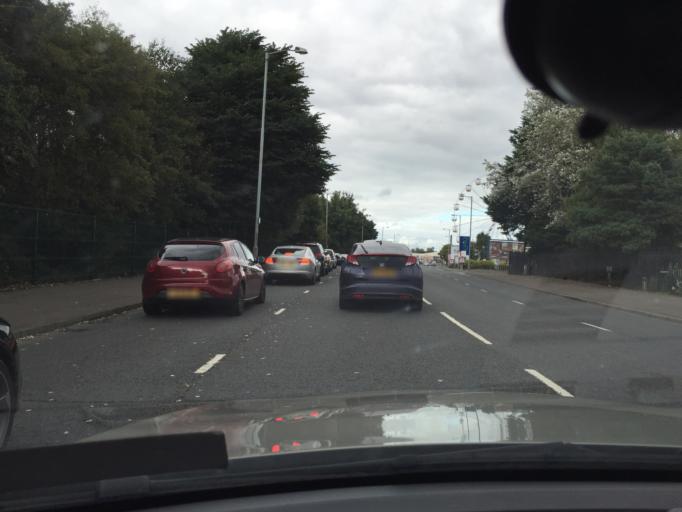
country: GB
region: Northern Ireland
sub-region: City of Belfast
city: Belfast
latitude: 54.5738
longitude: -5.9683
